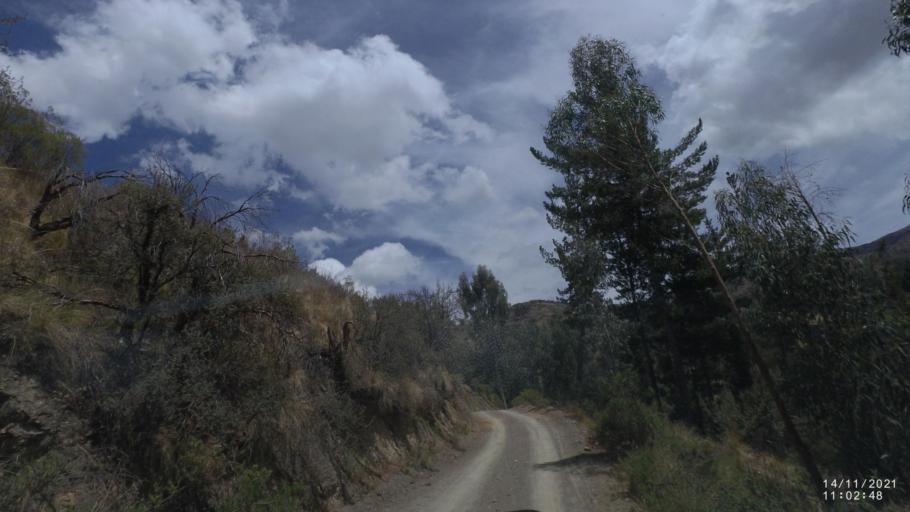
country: BO
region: Cochabamba
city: Cochabamba
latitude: -17.3384
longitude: -66.0593
